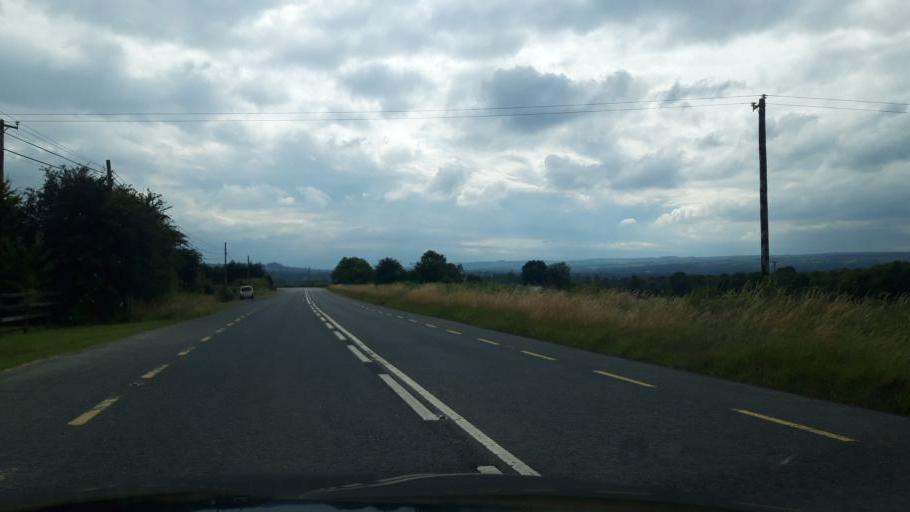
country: IE
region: Leinster
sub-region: Kilkenny
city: Castlecomer
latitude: 52.8577
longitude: -7.1148
